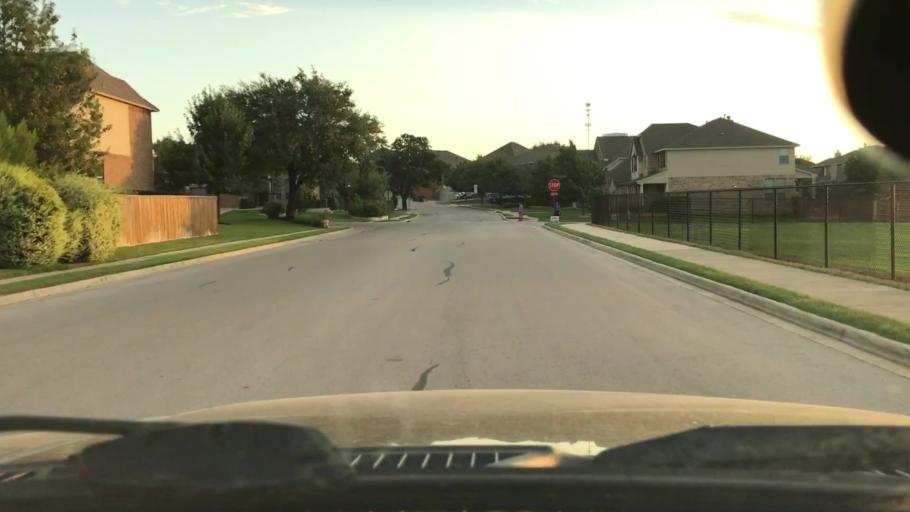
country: US
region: Texas
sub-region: Williamson County
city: Leander
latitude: 30.5390
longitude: -97.8662
